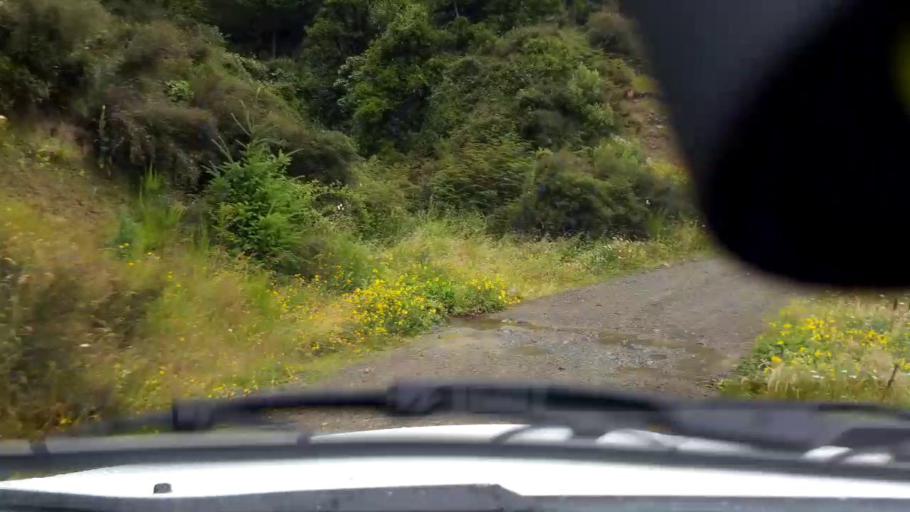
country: NZ
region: Canterbury
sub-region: Timaru District
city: Pleasant Point
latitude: -44.0352
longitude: 171.0071
